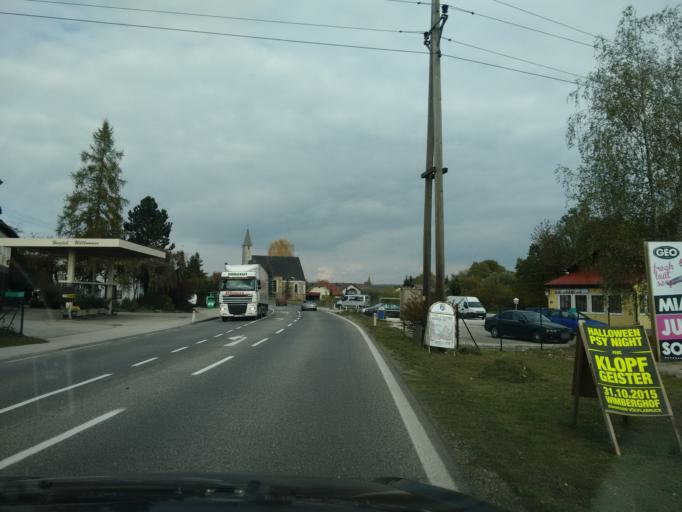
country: AT
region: Upper Austria
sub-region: Politischer Bezirk Vocklabruck
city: Lenzing
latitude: 47.9853
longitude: 13.6148
